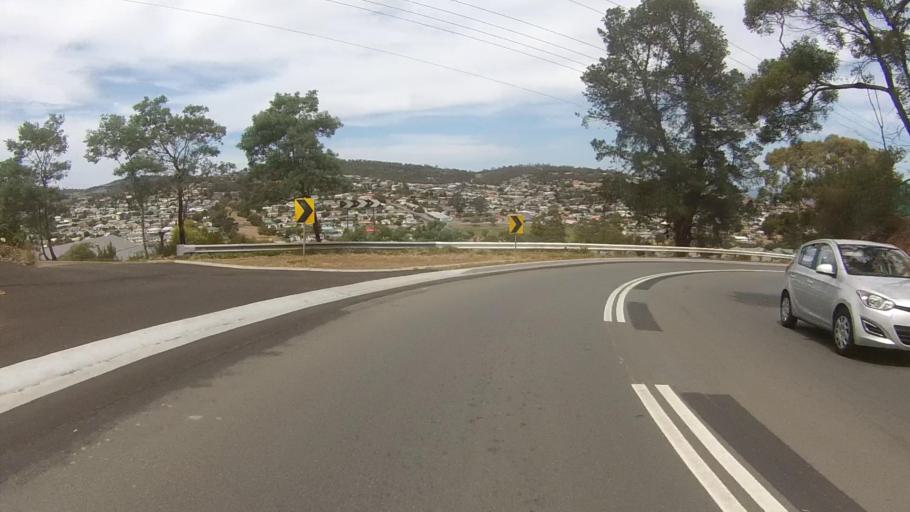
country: AU
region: Tasmania
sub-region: Clarence
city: Warrane
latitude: -42.8555
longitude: 147.3725
